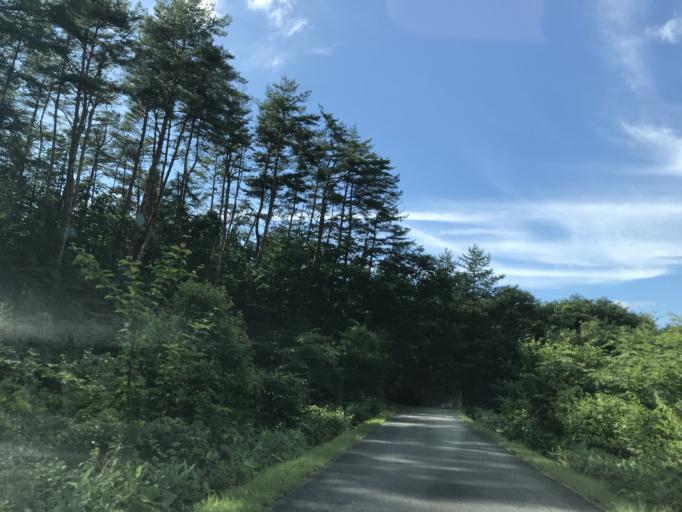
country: JP
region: Iwate
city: Ichinoseki
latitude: 38.9257
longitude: 140.9559
